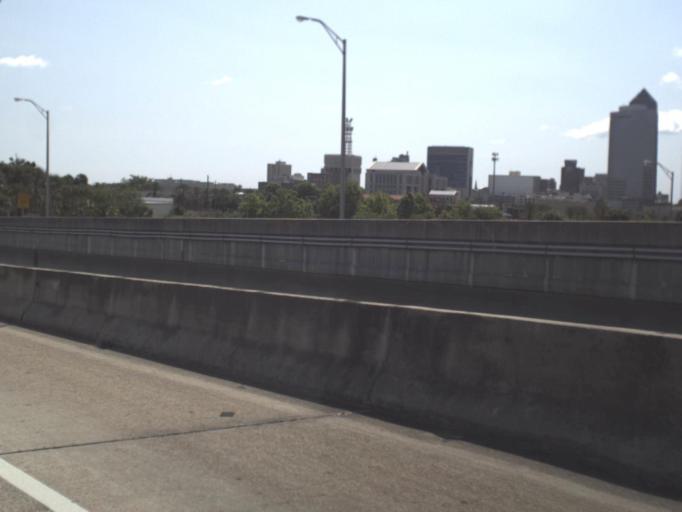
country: US
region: Florida
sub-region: Duval County
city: Jacksonville
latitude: 30.3298
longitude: -81.6754
